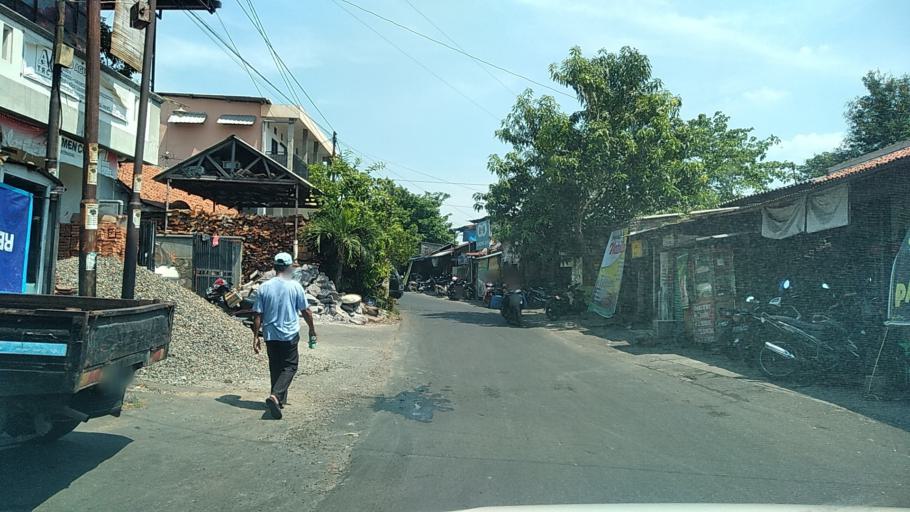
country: ID
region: Central Java
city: Semarang
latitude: -7.0130
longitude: 110.4413
